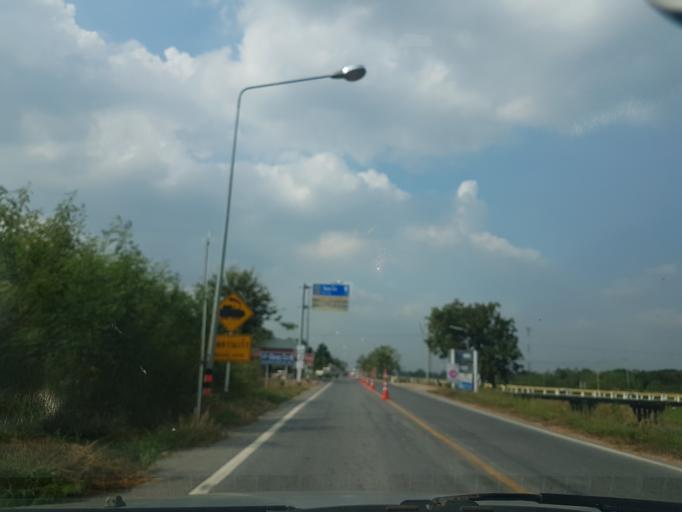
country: TH
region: Phra Nakhon Si Ayutthaya
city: Phachi
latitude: 14.4663
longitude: 100.7510
